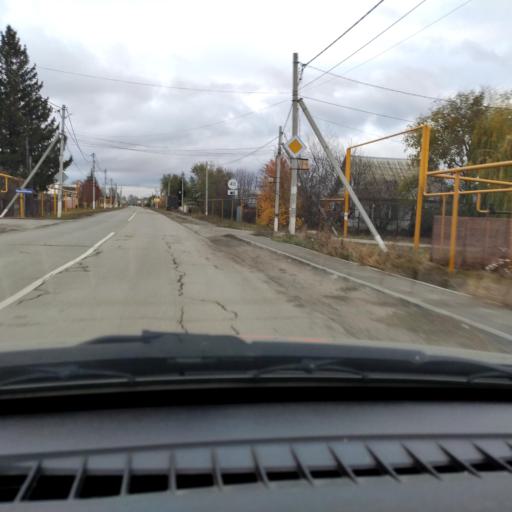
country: RU
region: Samara
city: Podstepki
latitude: 53.5160
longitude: 49.1274
